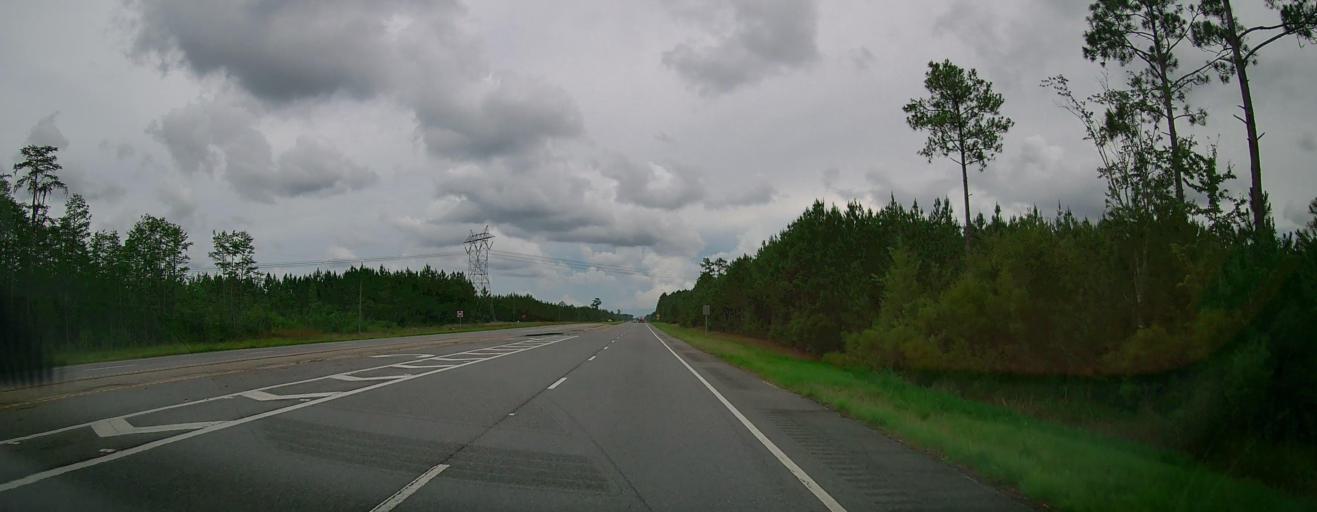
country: US
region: Georgia
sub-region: Wayne County
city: Jesup
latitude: 31.6797
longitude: -82.0881
